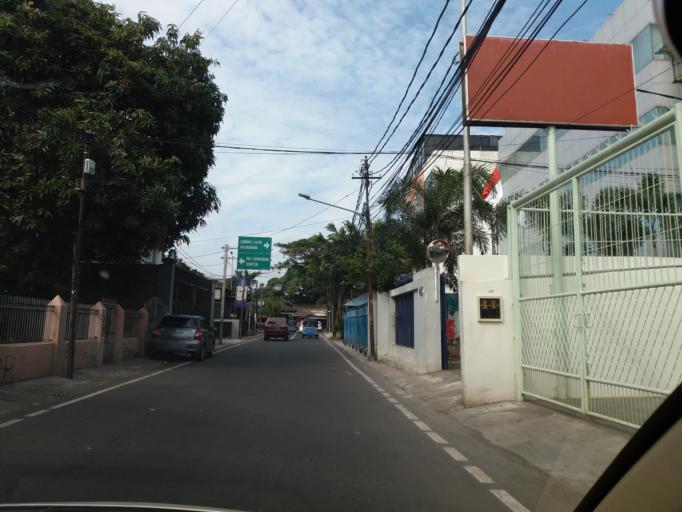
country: ID
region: Jakarta Raya
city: Jakarta
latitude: -6.1717
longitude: 106.8422
